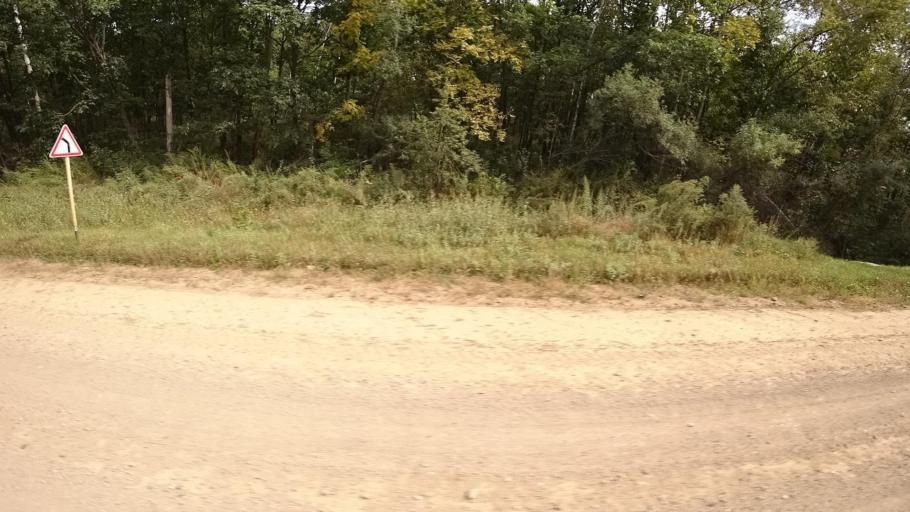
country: RU
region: Primorskiy
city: Yakovlevka
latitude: 44.4970
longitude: 133.5896
